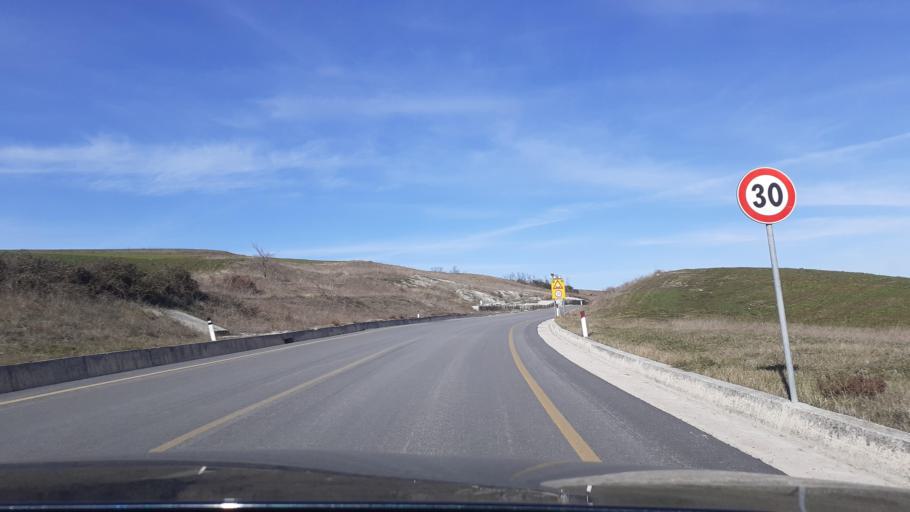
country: IT
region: Molise
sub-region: Provincia di Campobasso
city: Pietracupa
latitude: 41.6887
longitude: 14.5097
